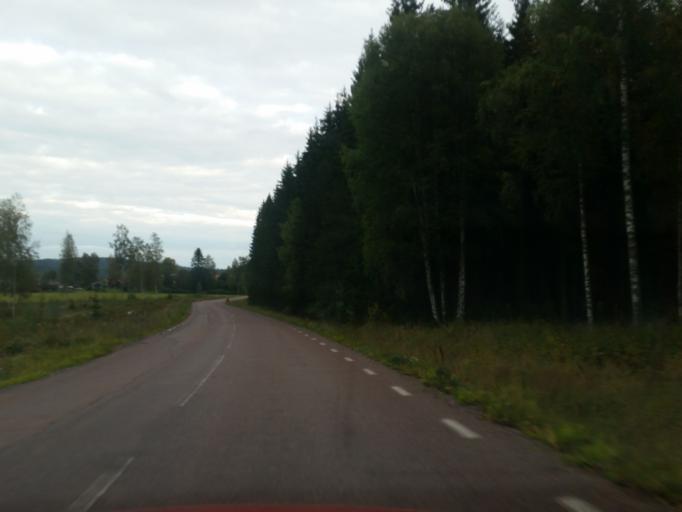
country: SE
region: Dalarna
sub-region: Leksand Municipality
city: Smedby
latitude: 60.6728
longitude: 15.1367
